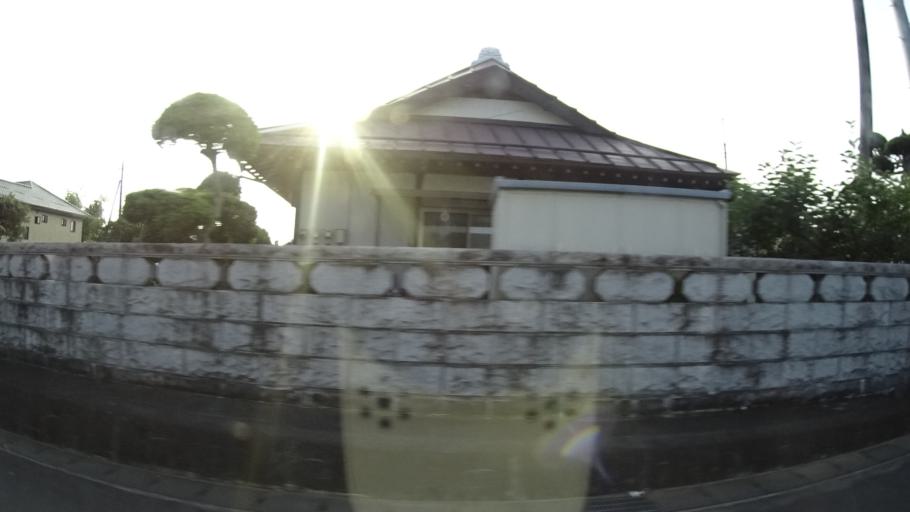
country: JP
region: Tochigi
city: Karasuyama
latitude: 36.6355
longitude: 140.1522
